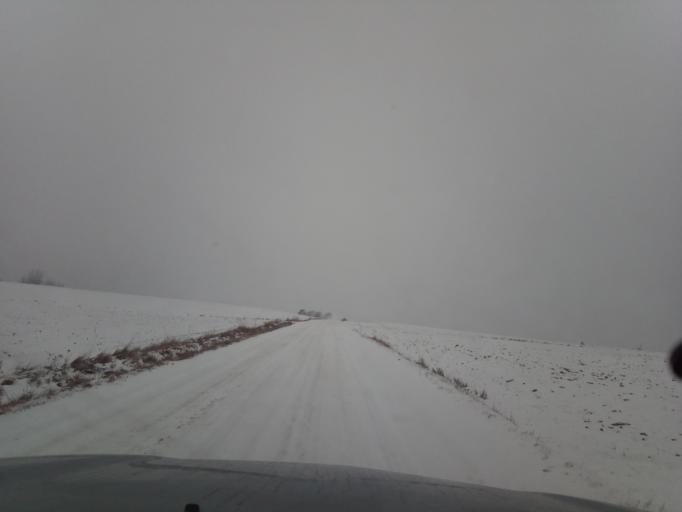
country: LT
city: Ramygala
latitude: 55.5655
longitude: 24.3368
